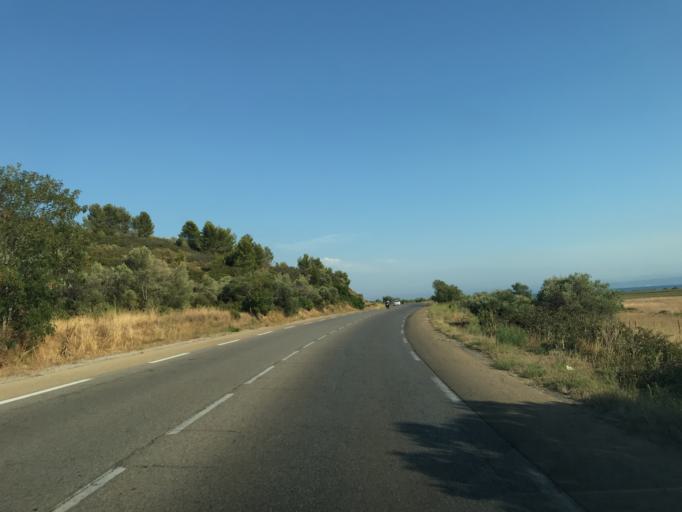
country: FR
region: Provence-Alpes-Cote d'Azur
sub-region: Departement des Bouches-du-Rhone
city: Saint-Chamas
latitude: 43.5325
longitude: 5.0503
